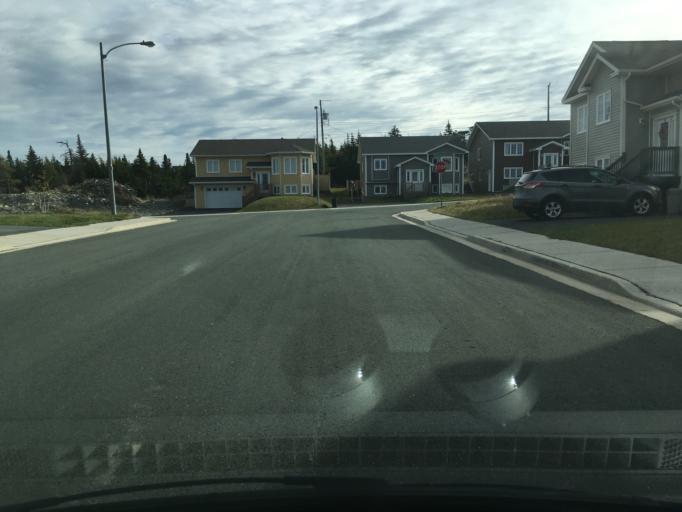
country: CA
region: Newfoundland and Labrador
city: Mount Pearl
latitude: 47.5546
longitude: -52.7906
